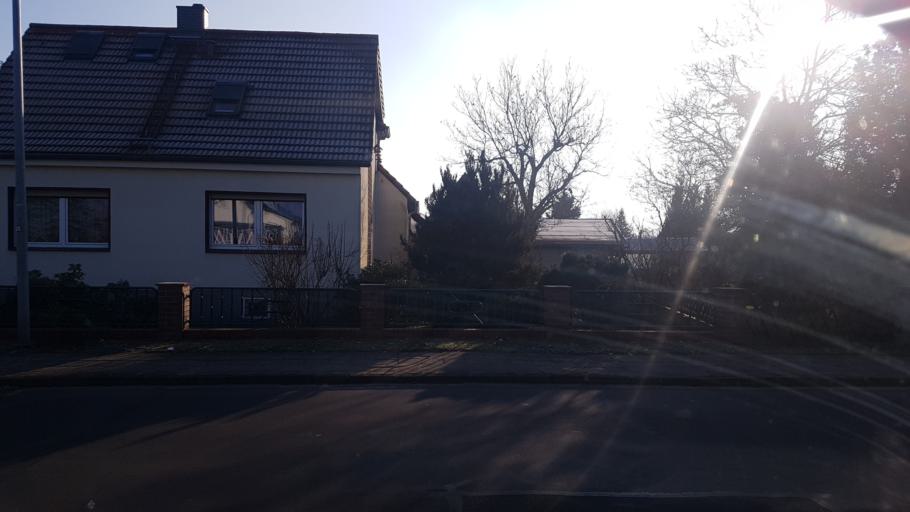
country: DE
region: Brandenburg
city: Lauchhammer
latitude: 51.4711
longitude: 13.7678
